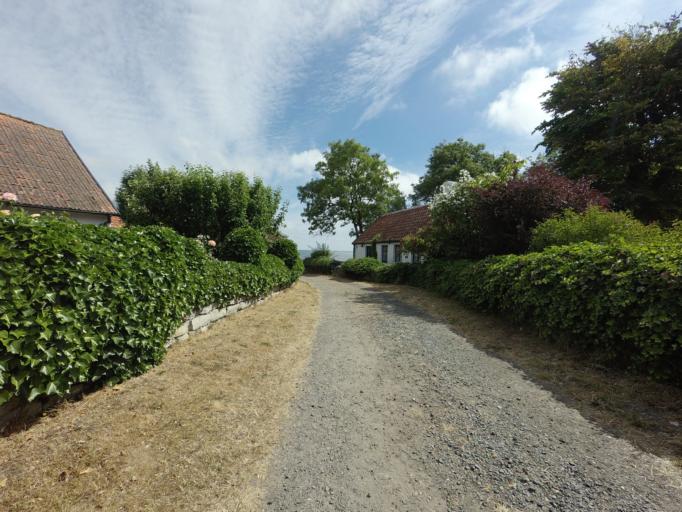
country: SE
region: Skane
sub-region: Simrishamns Kommun
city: Simrishamn
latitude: 55.4871
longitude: 14.3165
